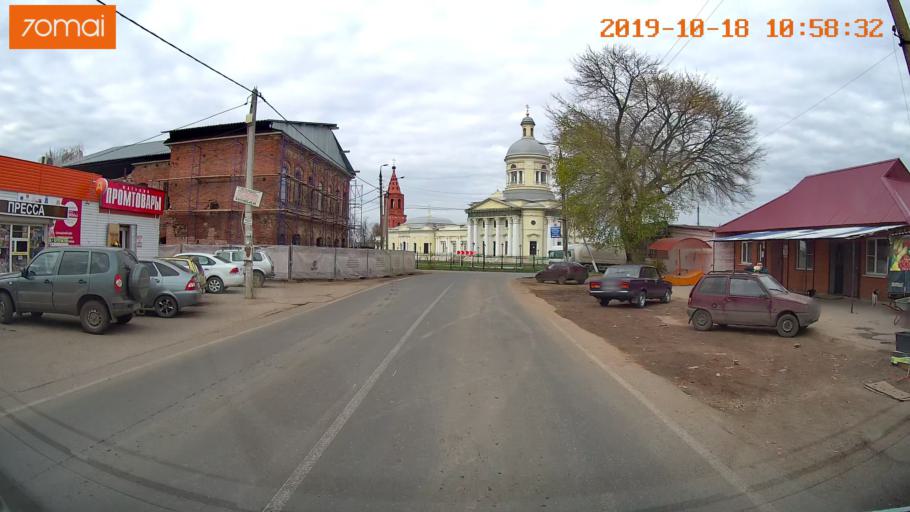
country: RU
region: Tula
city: Yepifan'
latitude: 53.8251
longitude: 38.5543
